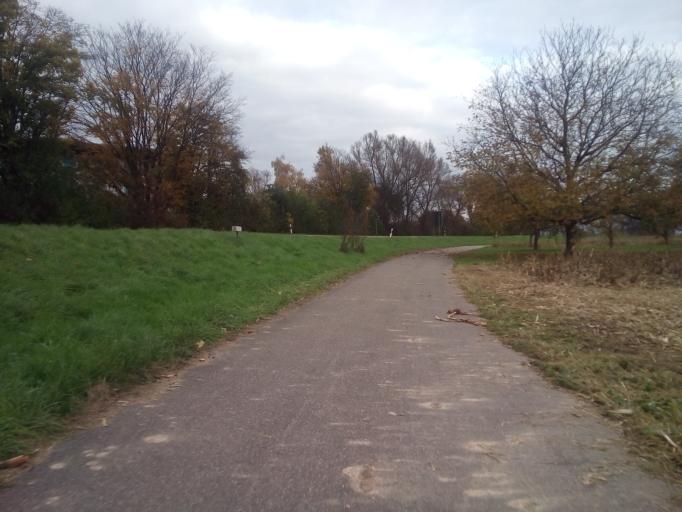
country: DE
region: Baden-Wuerttemberg
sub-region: Karlsruhe Region
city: Rheinmuenster
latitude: 48.7515
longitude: 8.0149
